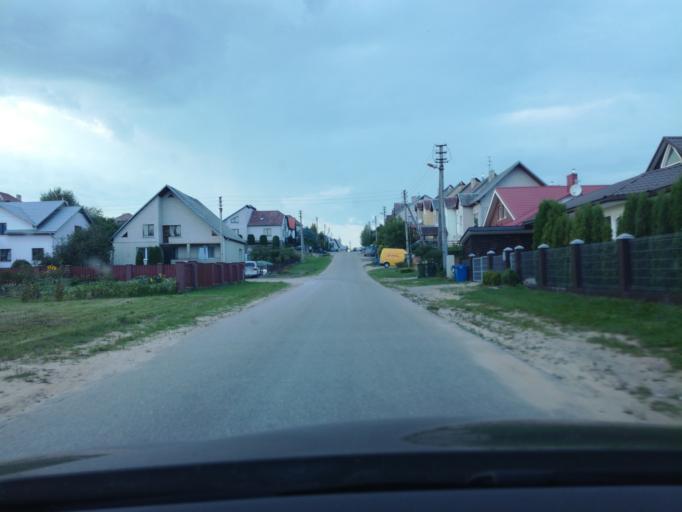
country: LT
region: Alytaus apskritis
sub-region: Alytus
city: Alytus
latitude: 54.3930
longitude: 24.0034
